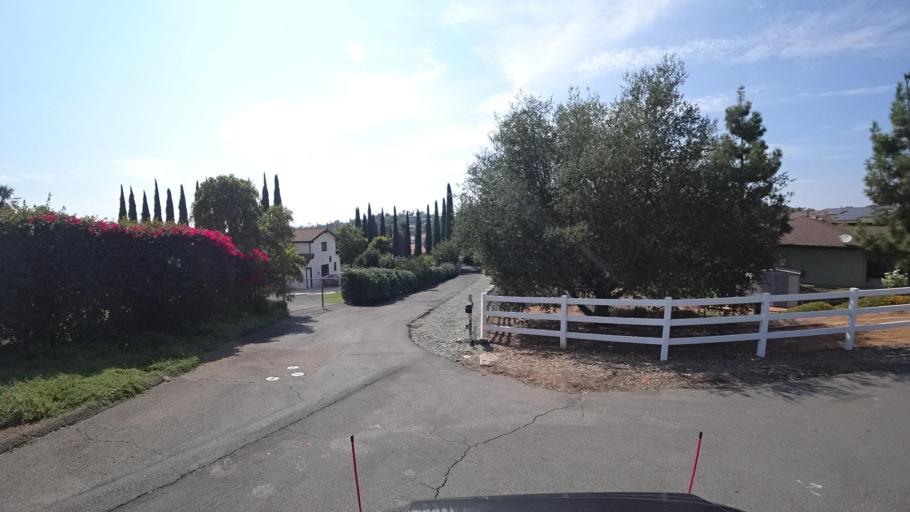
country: US
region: California
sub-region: San Diego County
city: Escondido
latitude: 33.1146
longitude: -117.0544
